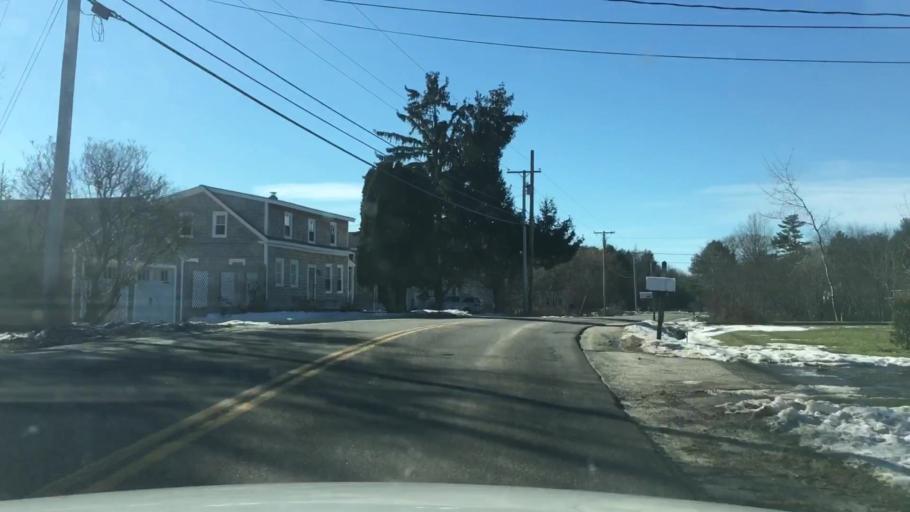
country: US
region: Maine
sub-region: Cumberland County
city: Brunswick
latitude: 43.8697
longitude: -69.9710
